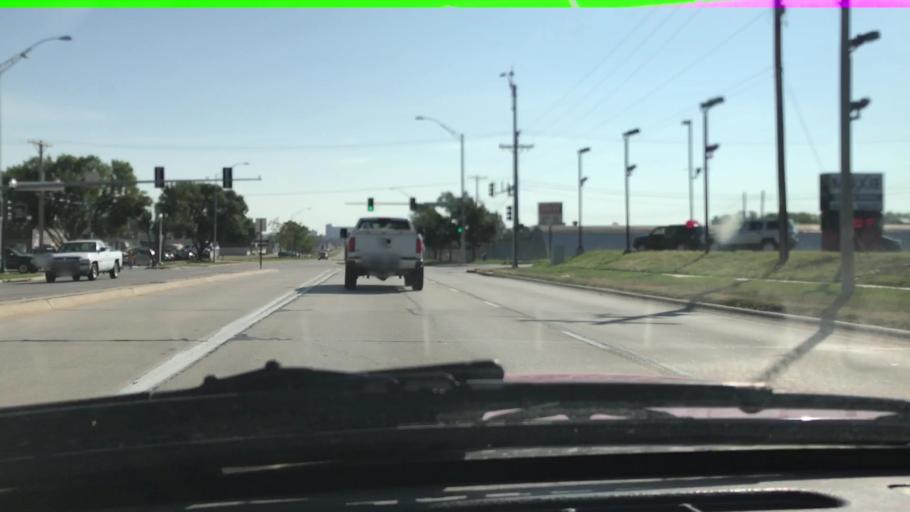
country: US
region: Nebraska
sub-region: Lancaster County
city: Lincoln
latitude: 40.8137
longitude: -96.7405
